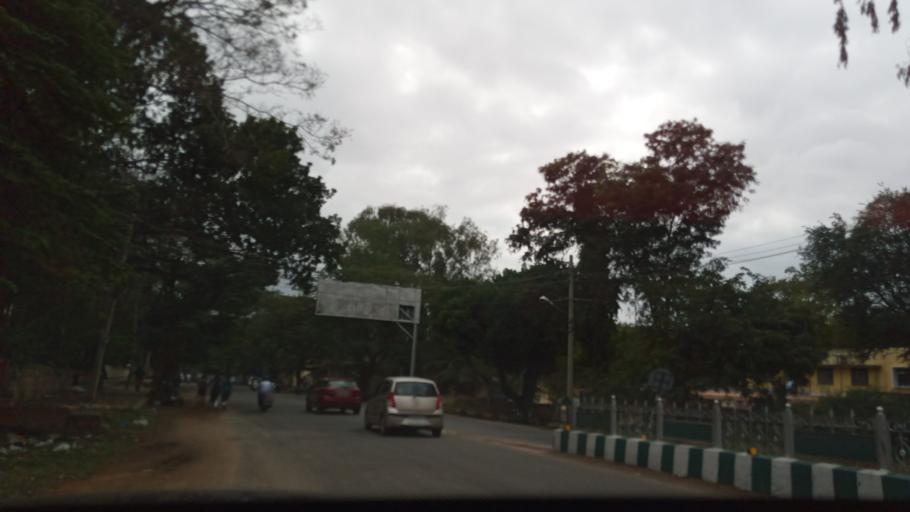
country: IN
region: Karnataka
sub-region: Mysore
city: Mysore
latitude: 12.3069
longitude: 76.6358
